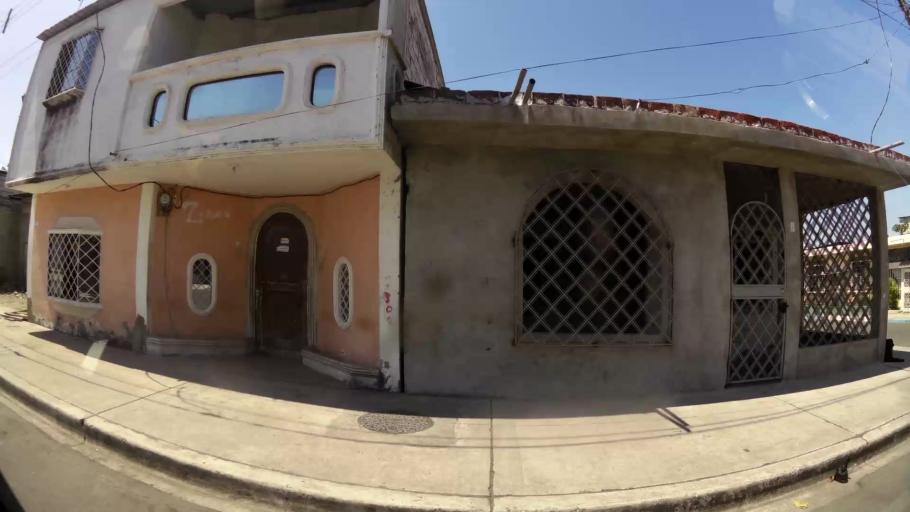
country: EC
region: Guayas
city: Guayaquil
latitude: -2.2323
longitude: -79.9198
